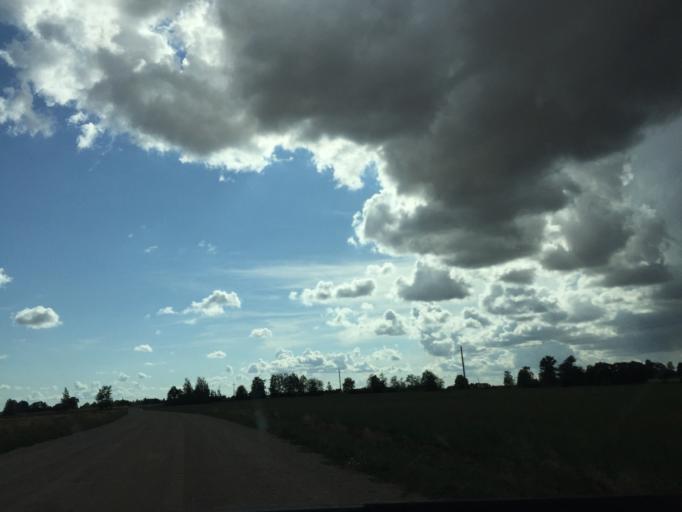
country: LV
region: Tervete
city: Zelmeni
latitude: 56.3025
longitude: 23.4122
